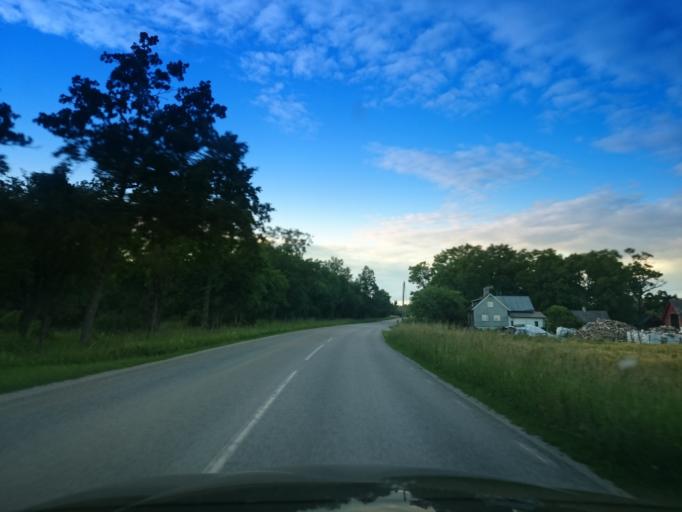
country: SE
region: Gotland
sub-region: Gotland
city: Hemse
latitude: 57.3096
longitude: 18.3801
